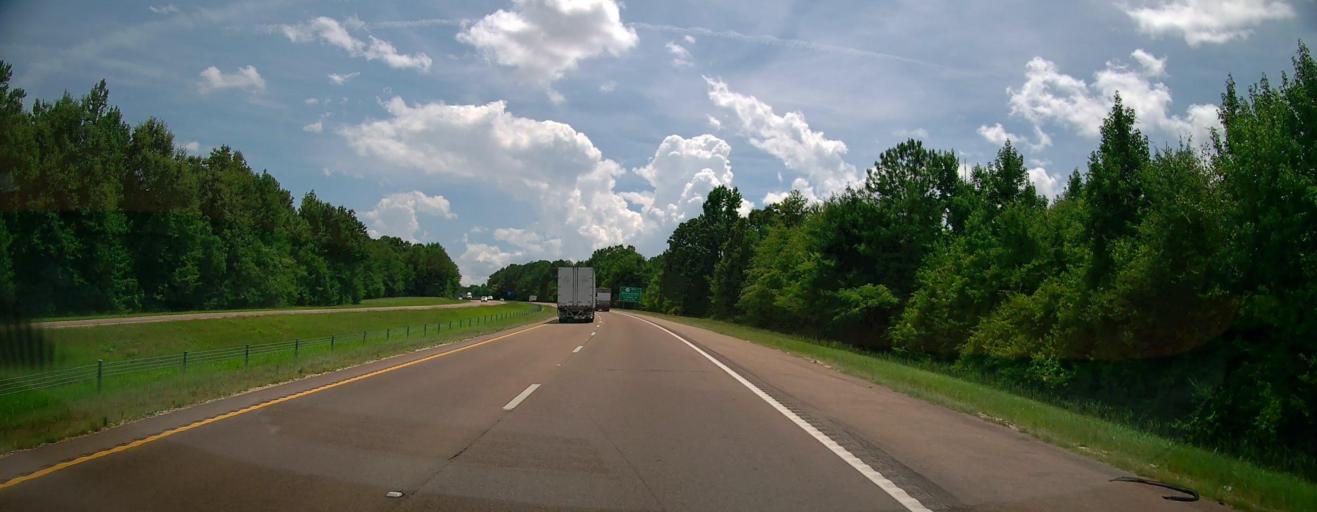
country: US
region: Mississippi
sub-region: Lee County
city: Tupelo
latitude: 34.2851
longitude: -88.7076
